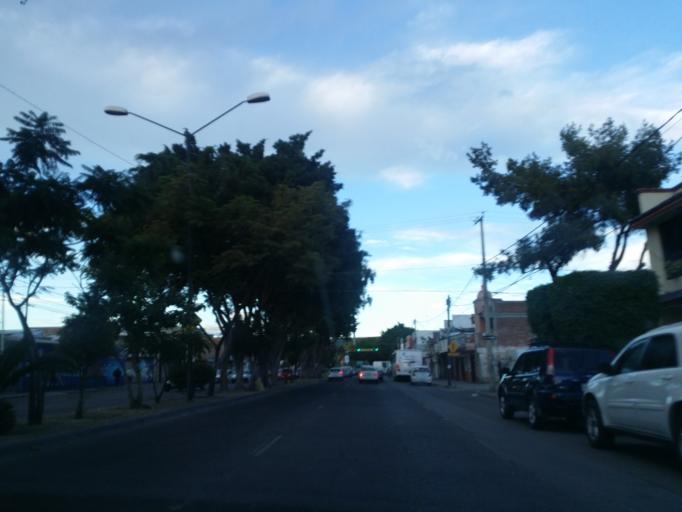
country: MX
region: Guanajuato
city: Leon
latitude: 21.1448
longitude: -101.6523
